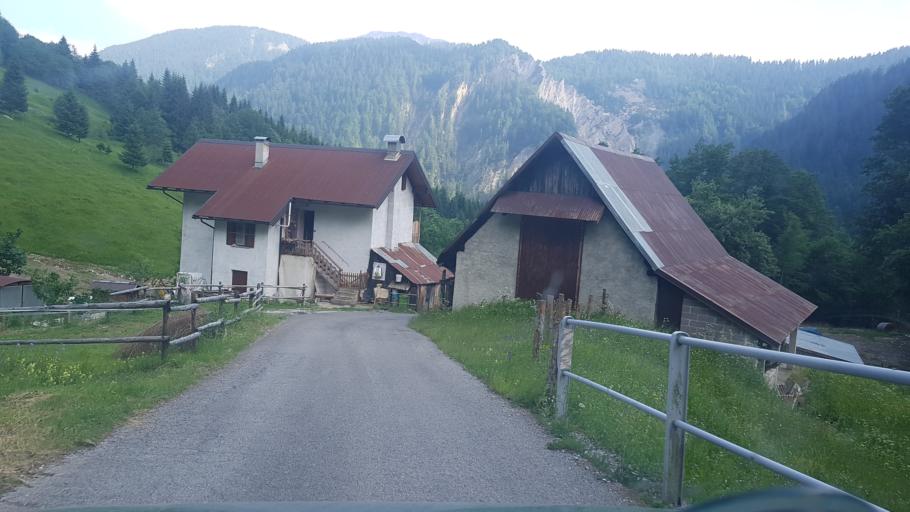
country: IT
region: Friuli Venezia Giulia
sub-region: Provincia di Udine
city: Paularo
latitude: 46.5328
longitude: 13.2099
